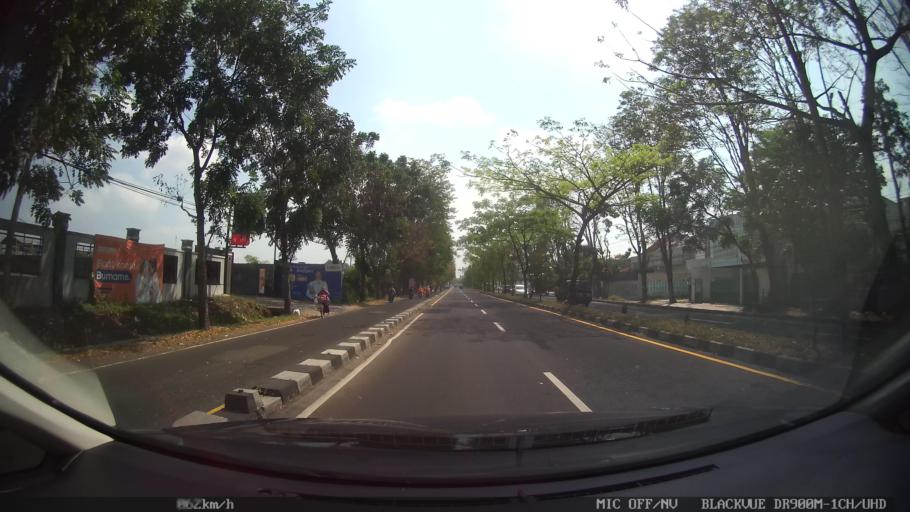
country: ID
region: Daerah Istimewa Yogyakarta
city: Yogyakarta
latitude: -7.7625
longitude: 110.3365
